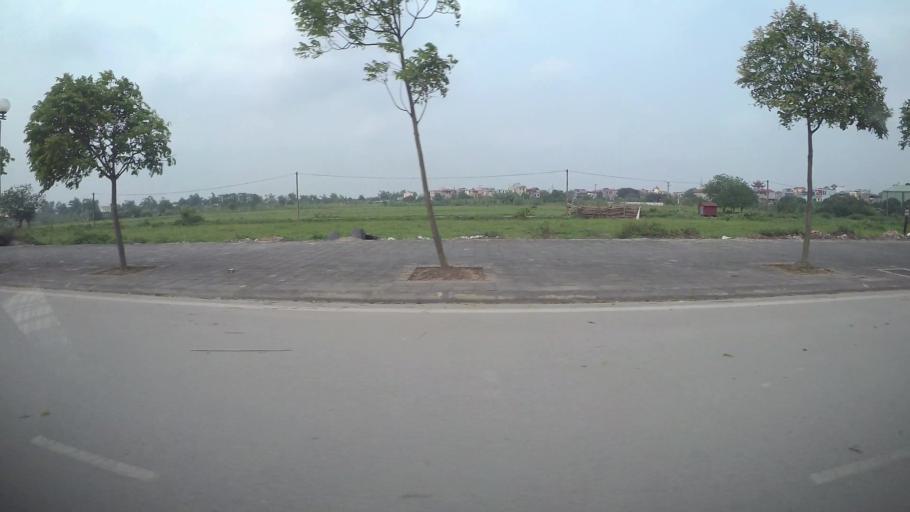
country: VN
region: Ha Noi
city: Hoan Kiem
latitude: 21.0733
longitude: 105.8982
